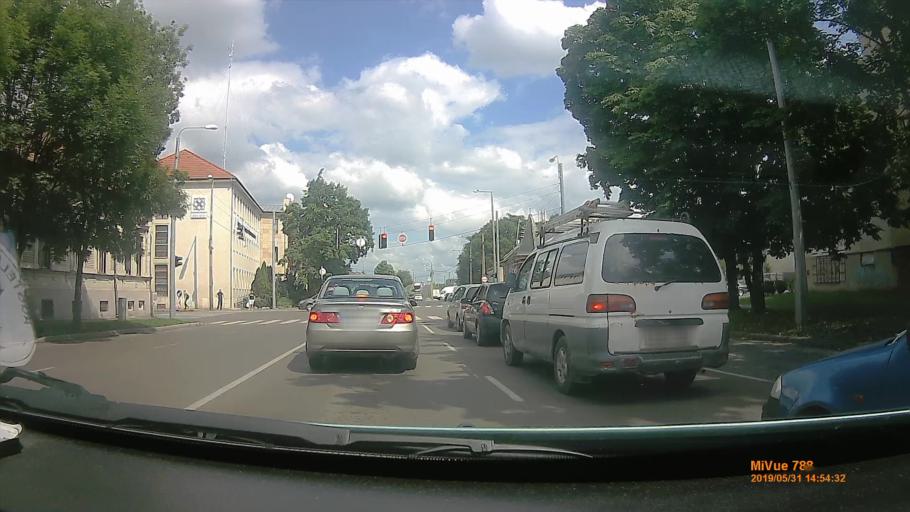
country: HU
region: Borsod-Abauj-Zemplen
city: Miskolc
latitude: 48.0994
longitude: 20.7972
